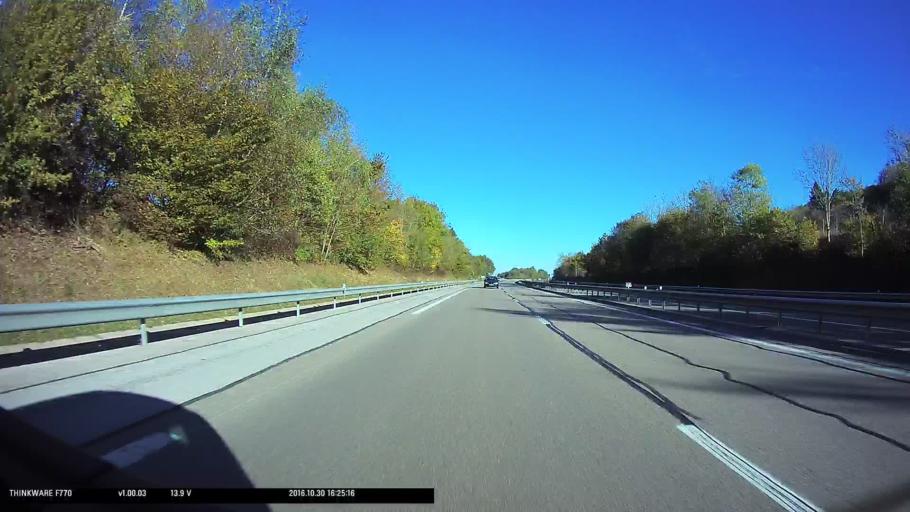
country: FR
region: Franche-Comte
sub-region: Departement du Doubs
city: Baume-les-Dames
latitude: 47.3741
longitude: 6.3512
